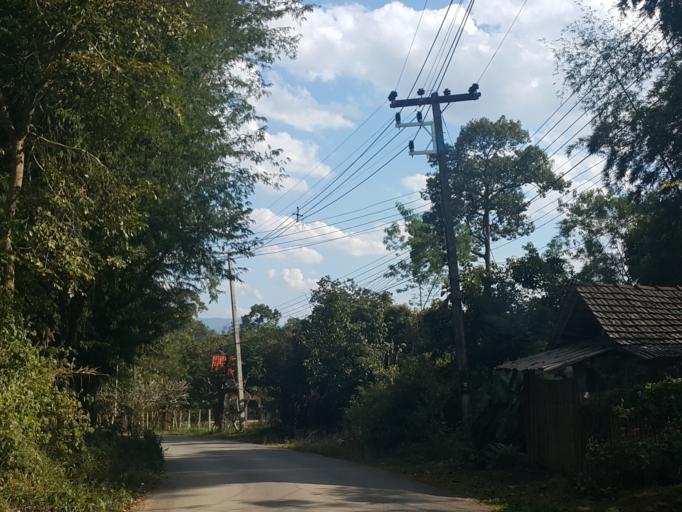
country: TH
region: Chiang Mai
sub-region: Amphoe Chiang Dao
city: Chiang Dao
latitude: 19.4009
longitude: 98.9258
